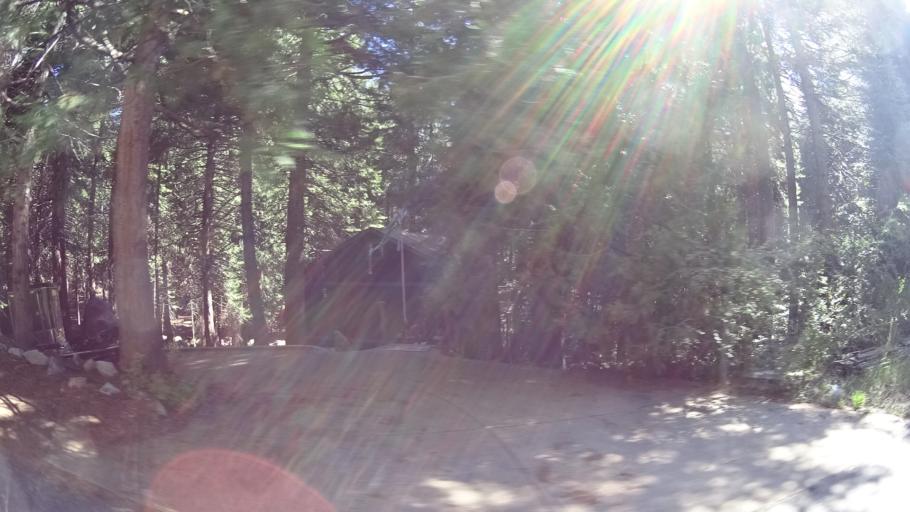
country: US
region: California
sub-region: Calaveras County
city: Arnold
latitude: 38.2889
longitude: -120.2792
